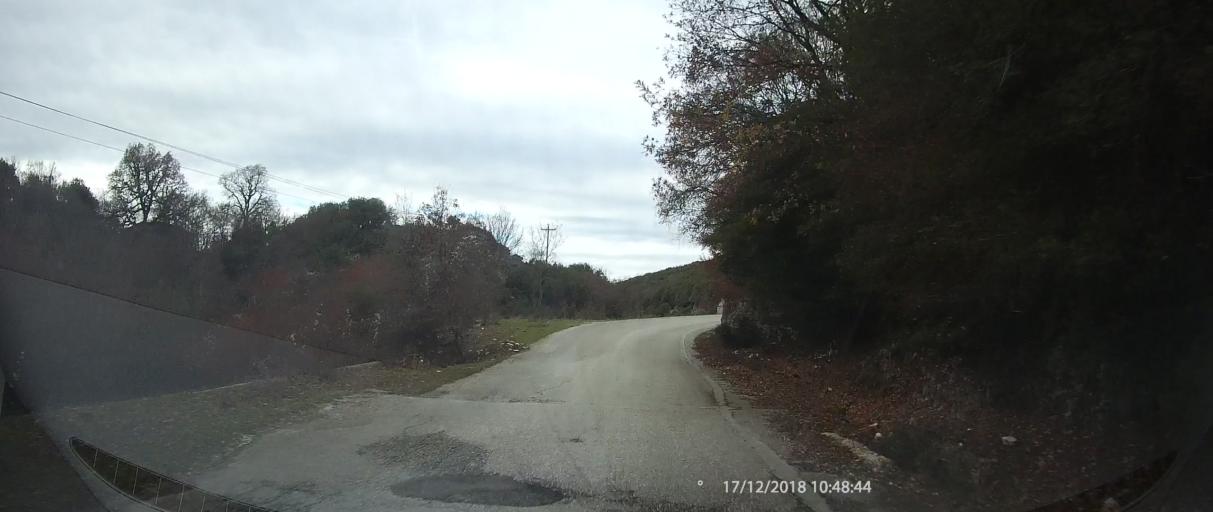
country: GR
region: Epirus
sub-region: Nomos Ioanninon
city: Konitsa
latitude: 39.9633
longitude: 20.7080
